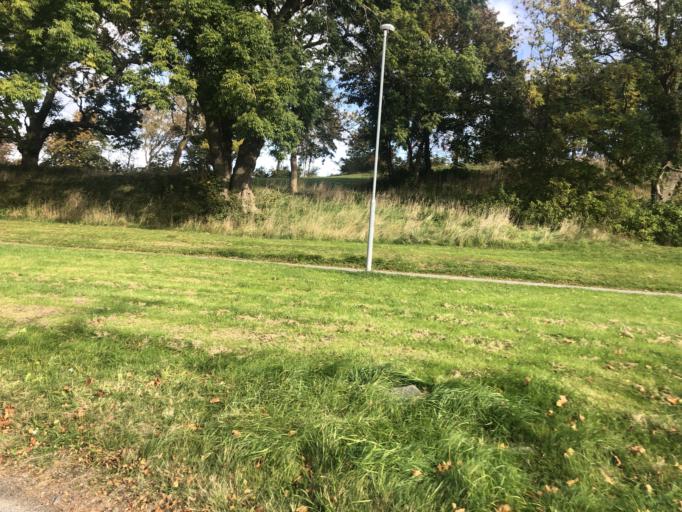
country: SE
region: Vaestra Goetaland
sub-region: Molndal
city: Moelndal
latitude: 57.6498
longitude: 12.0098
